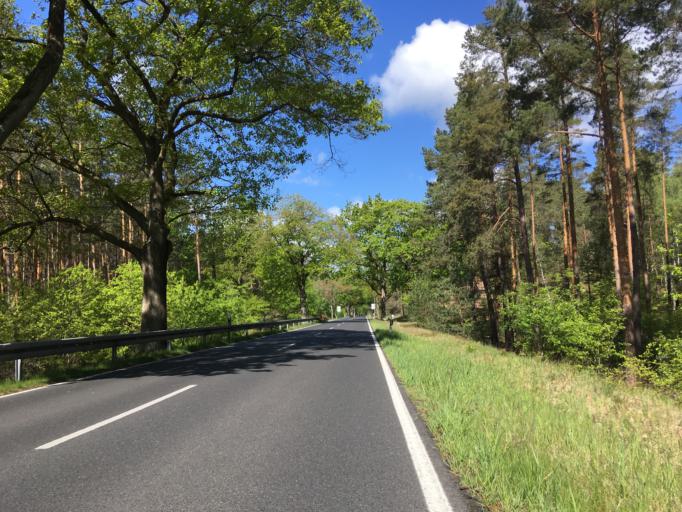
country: DE
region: Brandenburg
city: Birkenwerder
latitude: 52.7256
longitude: 13.3177
